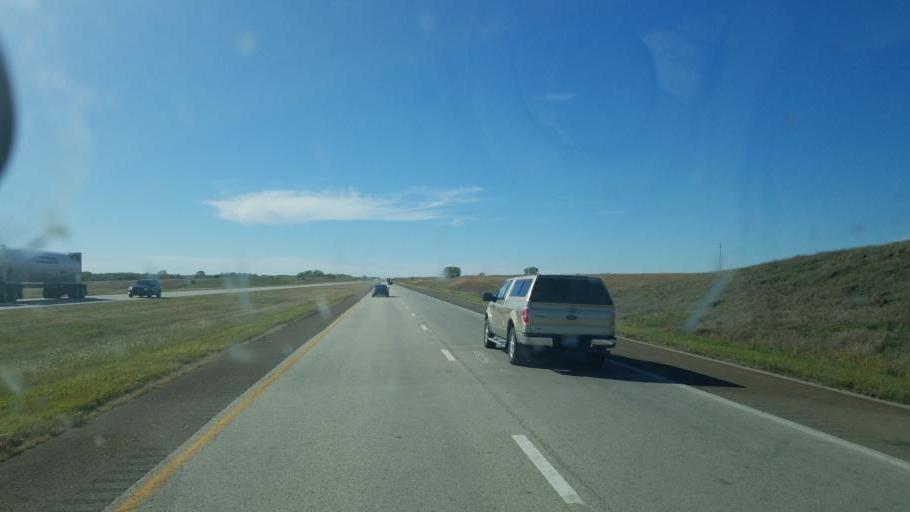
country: US
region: Kansas
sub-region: Saline County
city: Salina
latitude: 38.8779
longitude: -97.8288
